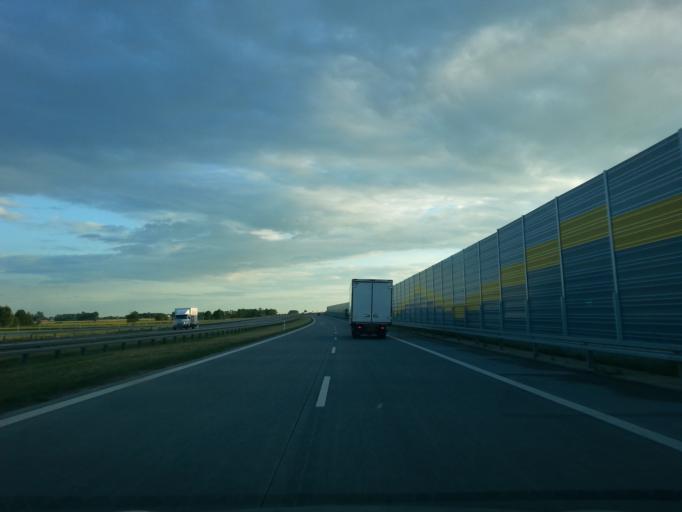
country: PL
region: Lodz Voivodeship
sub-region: Powiat wieruszowski
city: Lututow
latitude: 51.3262
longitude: 18.4411
